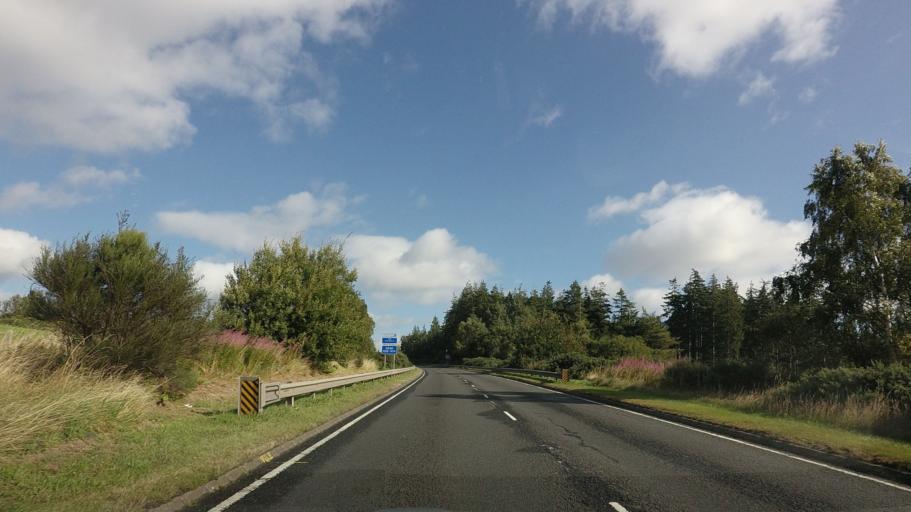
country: GB
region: Scotland
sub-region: Highland
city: Dingwall
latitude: 57.5512
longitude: -4.3361
